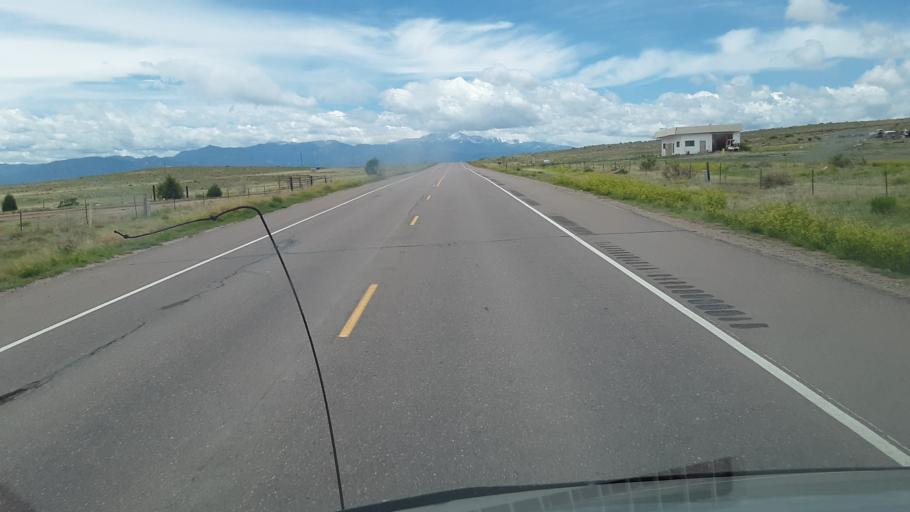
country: US
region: Colorado
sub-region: El Paso County
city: Cimarron Hills
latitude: 38.8387
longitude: -104.6003
